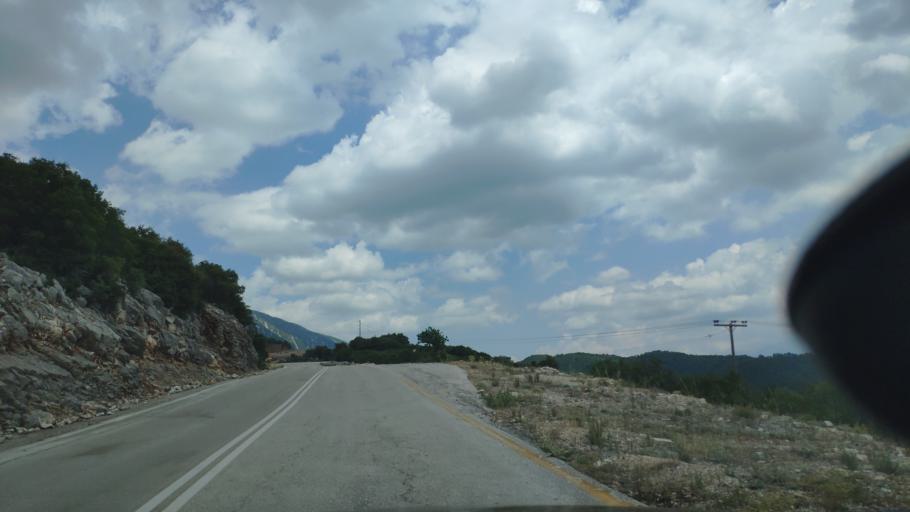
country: GR
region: Epirus
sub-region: Nomos Artas
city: Grammenitsa
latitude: 39.2794
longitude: 20.9761
